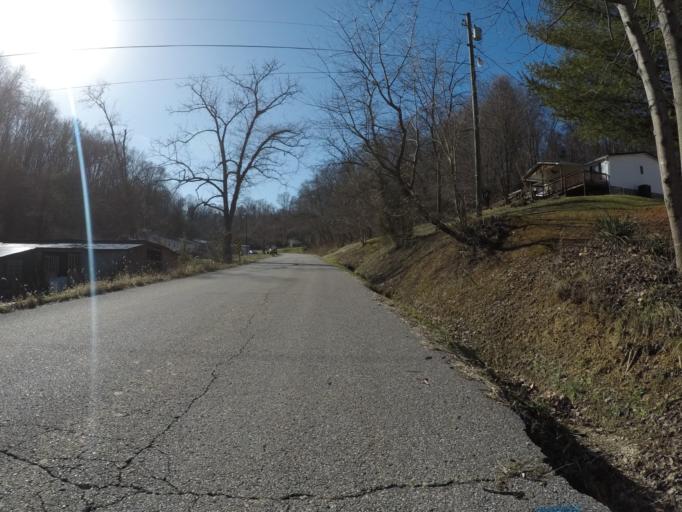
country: US
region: Kentucky
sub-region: Boyd County
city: Catlettsburg
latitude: 38.4041
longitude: -82.6289
